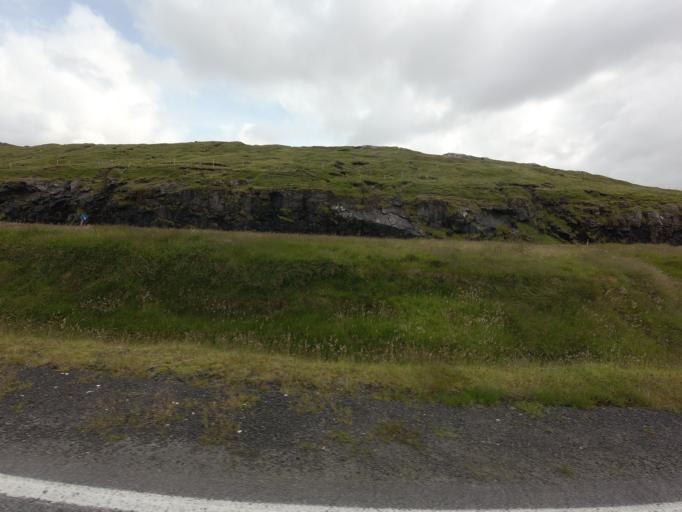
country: FO
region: Eysturoy
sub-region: Eidi
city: Eidi
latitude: 62.2228
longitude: -7.0049
